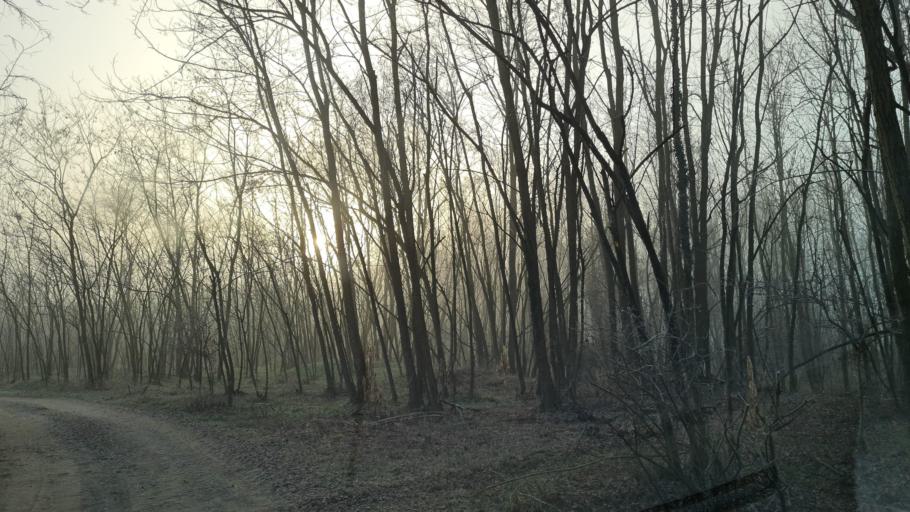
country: IT
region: Piedmont
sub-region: Provincia di Biella
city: Vergnasco
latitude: 45.4666
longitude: 8.0903
